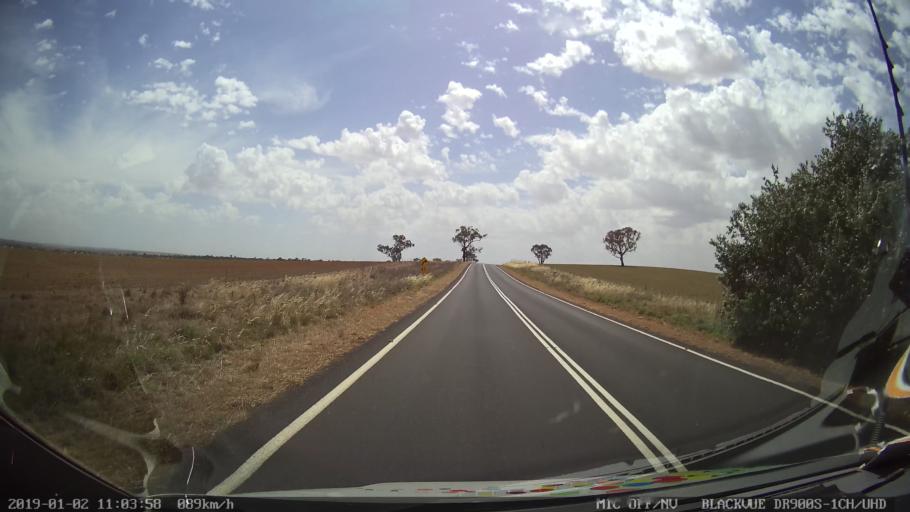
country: AU
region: New South Wales
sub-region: Young
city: Young
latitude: -34.5755
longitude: 148.3454
